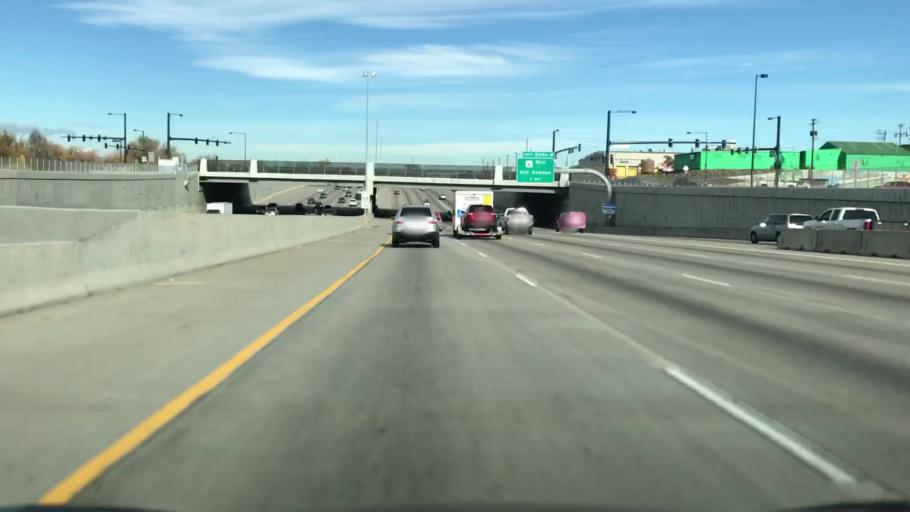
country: US
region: Colorado
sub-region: Denver County
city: Denver
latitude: 39.7098
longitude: -104.9982
